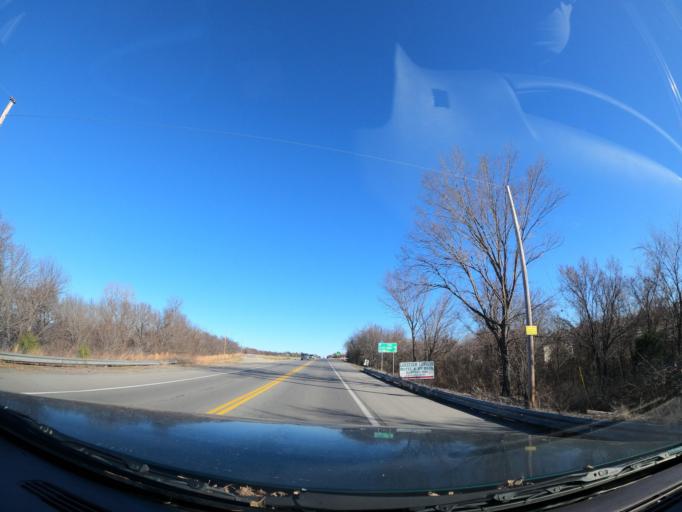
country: US
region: Oklahoma
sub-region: Pittsburg County
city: Longtown
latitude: 35.2391
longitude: -95.5513
